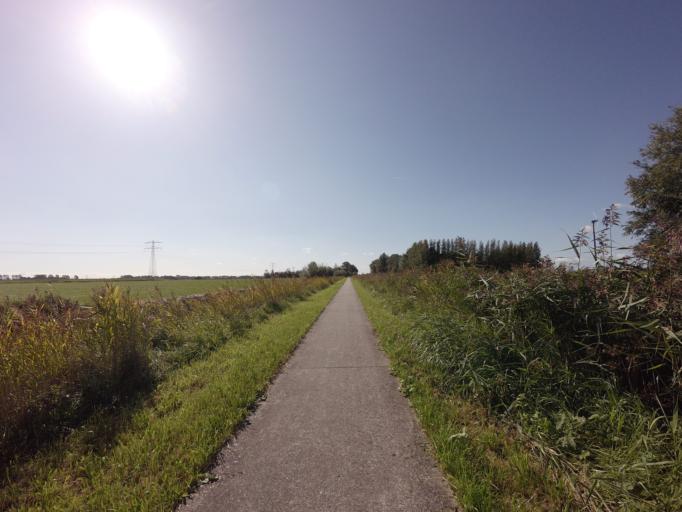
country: NL
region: Friesland
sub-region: Gemeente Leeuwarden
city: Wirdum
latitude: 53.1594
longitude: 5.7657
